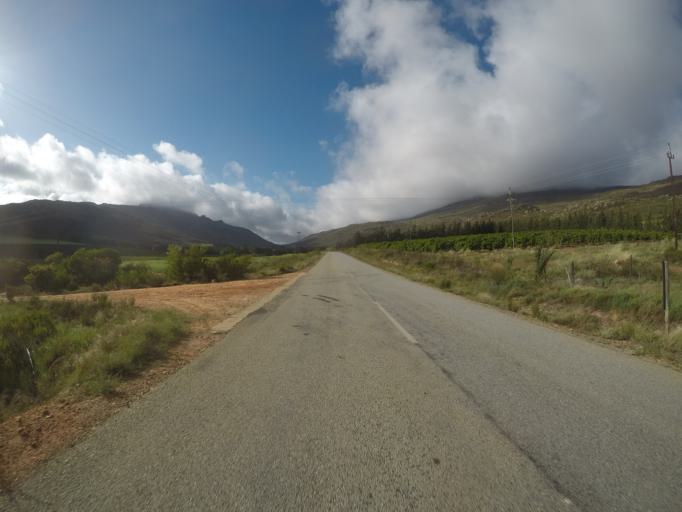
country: ZA
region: Western Cape
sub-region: West Coast District Municipality
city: Clanwilliam
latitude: -32.3546
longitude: 18.8504
